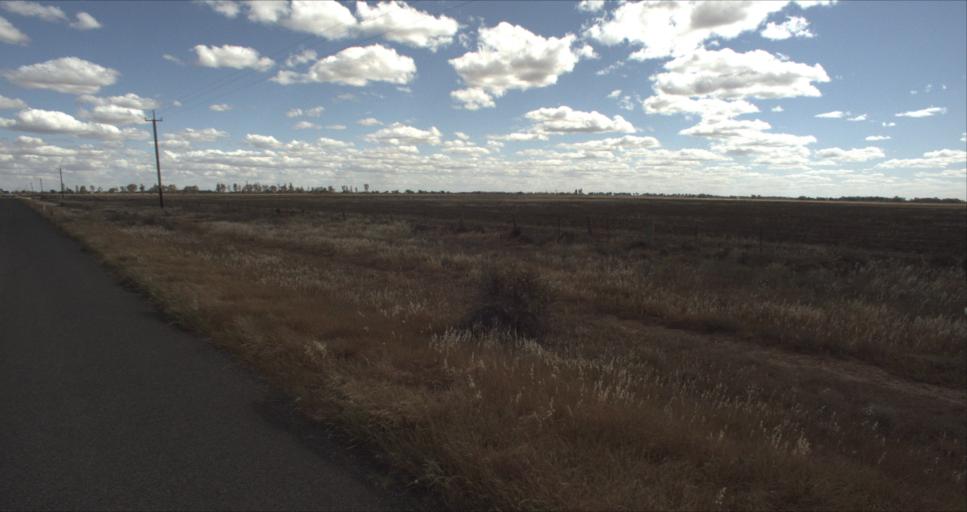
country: AU
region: New South Wales
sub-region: Leeton
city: Leeton
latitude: -34.4330
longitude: 146.2578
